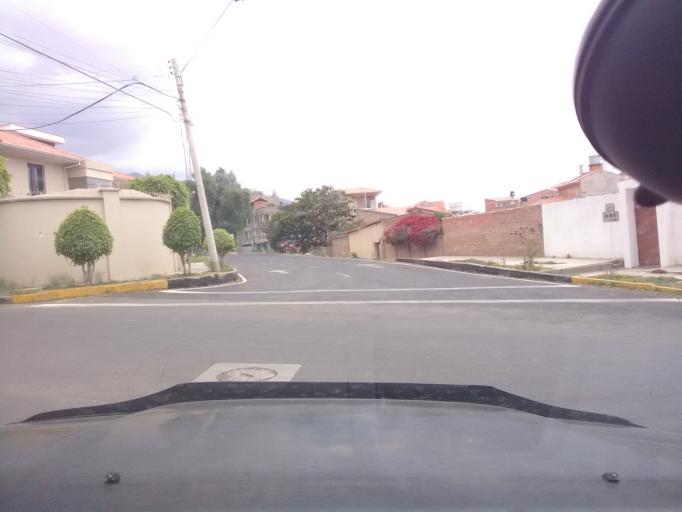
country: BO
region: Cochabamba
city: Cochabamba
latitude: -17.3648
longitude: -66.1707
